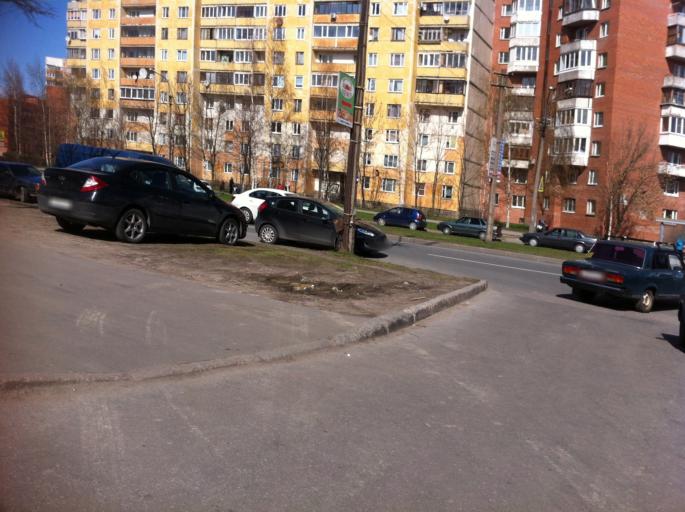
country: RU
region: St.-Petersburg
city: Uritsk
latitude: 59.8538
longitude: 30.1912
